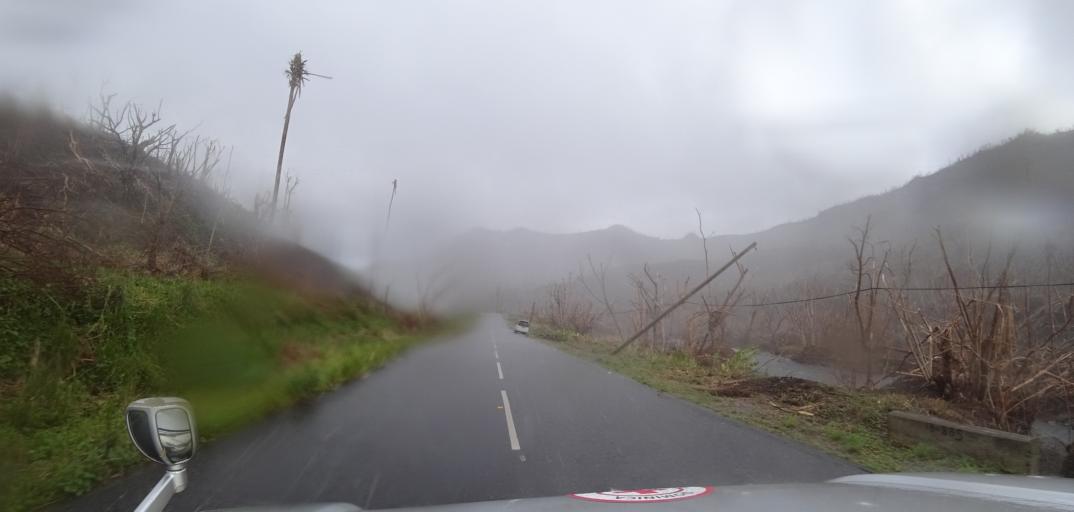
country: DM
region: Saint David
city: Castle Bruce
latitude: 15.4843
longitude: -61.2791
